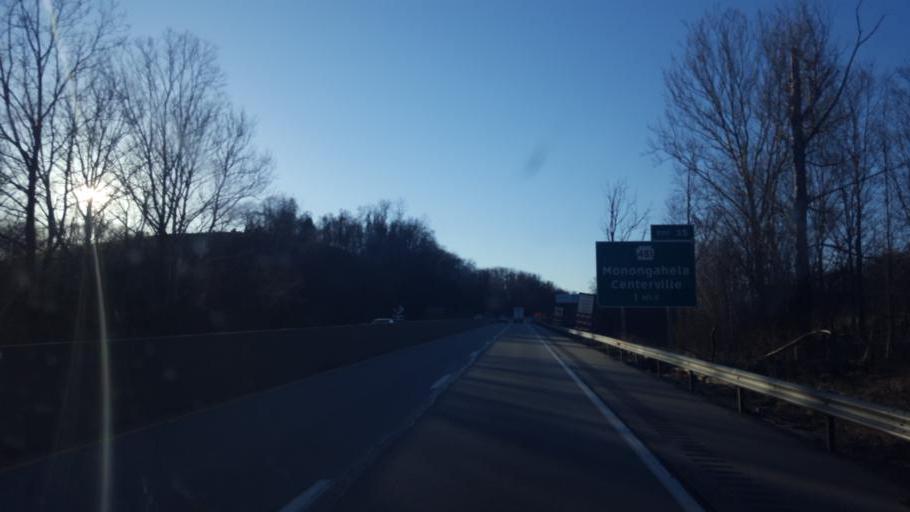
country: US
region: Pennsylvania
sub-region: Washington County
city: North Charleroi
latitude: 40.1157
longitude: -79.9443
